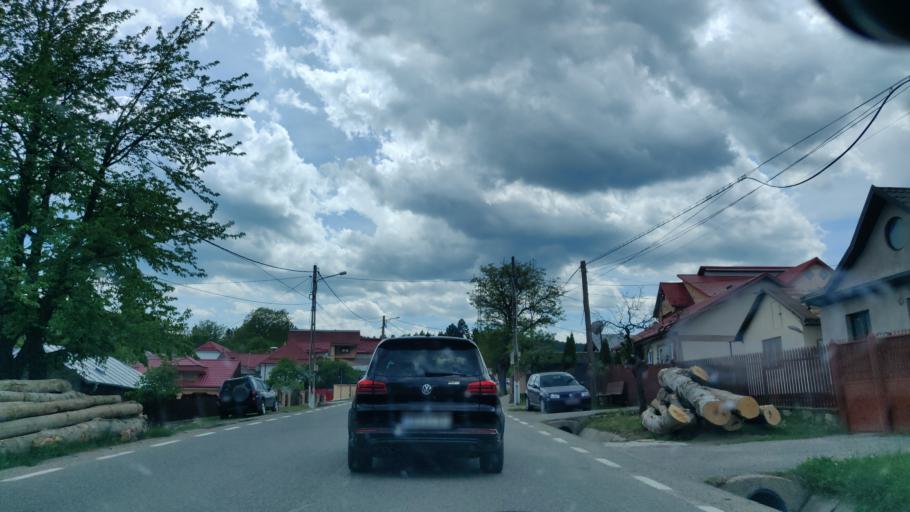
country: RO
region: Vrancea
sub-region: Comuna Tulnici
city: Tulnici
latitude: 45.9116
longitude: 26.6665
